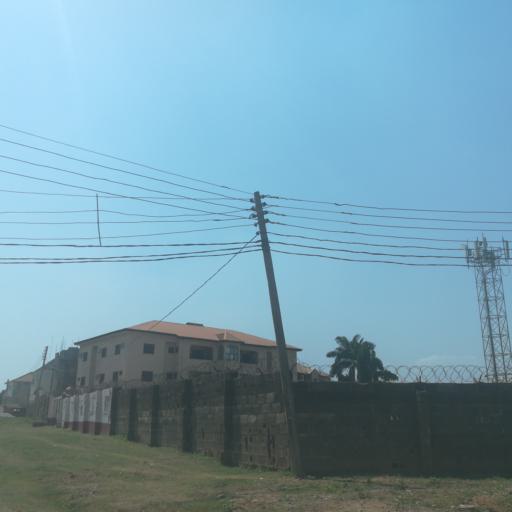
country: NG
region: Abuja Federal Capital Territory
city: Abuja
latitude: 9.0831
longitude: 7.4480
